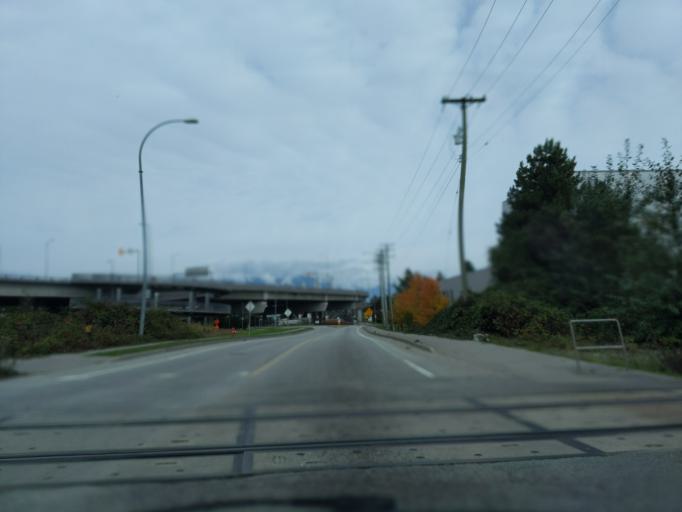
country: CA
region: British Columbia
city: Walnut Grove
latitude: 49.1832
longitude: -122.6643
